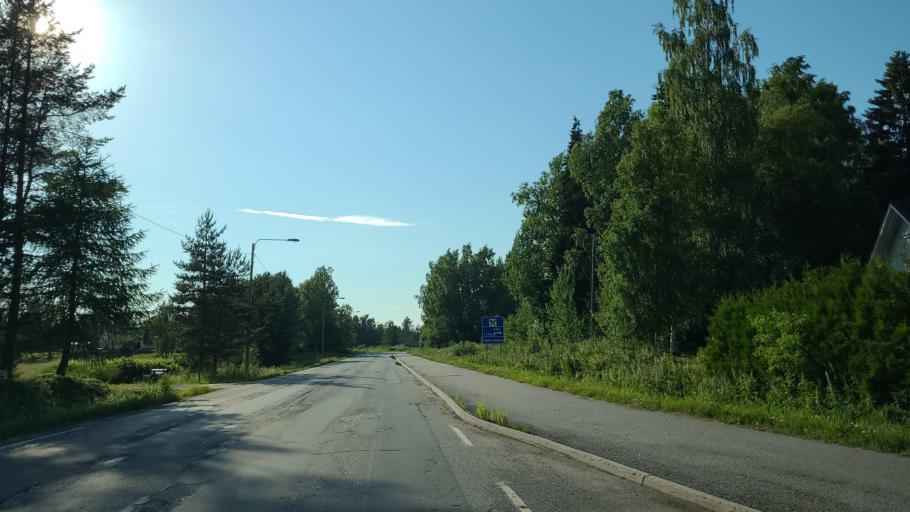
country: FI
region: Ostrobothnia
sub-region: Vaasa
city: Replot
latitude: 63.2192
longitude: 21.4202
